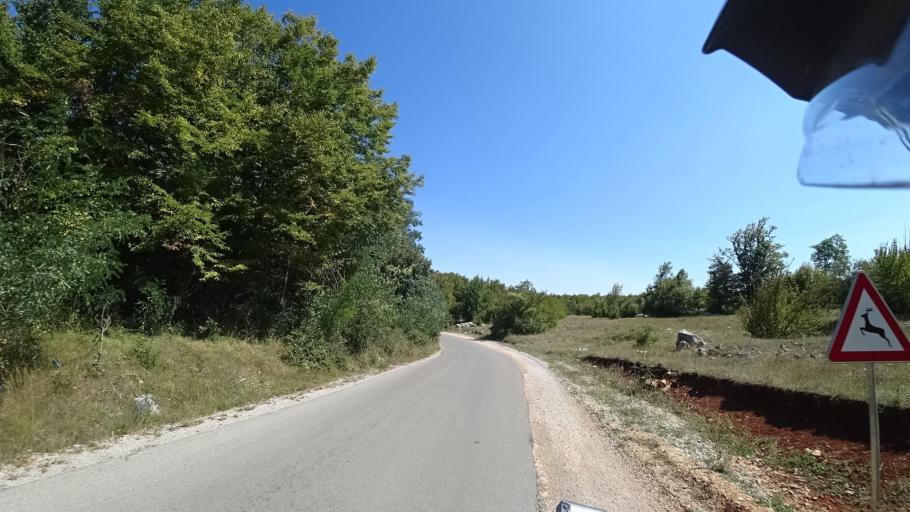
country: HR
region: Licko-Senjska
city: Popovaca
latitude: 44.7297
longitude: 15.2944
